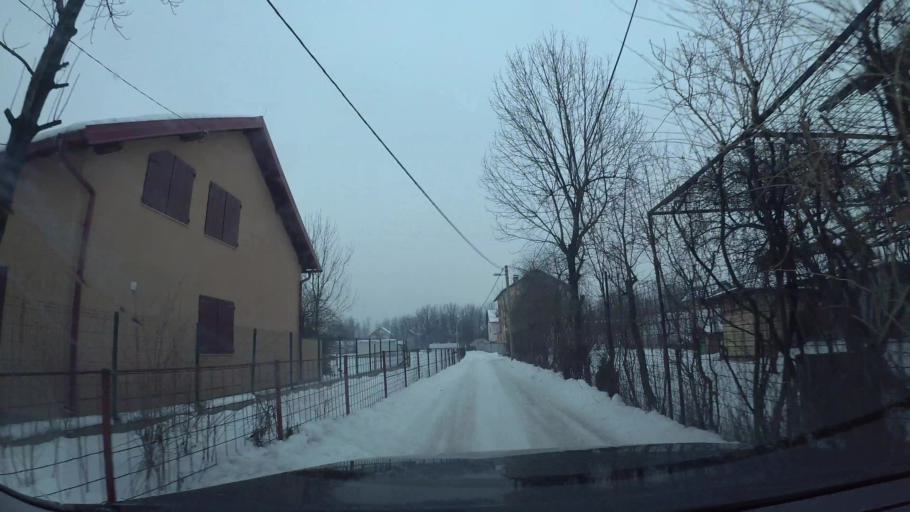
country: BA
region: Federation of Bosnia and Herzegovina
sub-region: Kanton Sarajevo
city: Sarajevo
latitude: 43.8417
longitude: 18.2952
